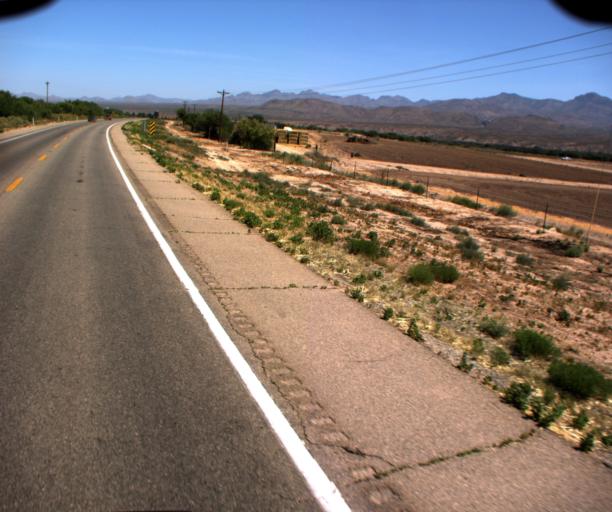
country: US
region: Arizona
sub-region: Graham County
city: Pima
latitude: 33.0228
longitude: -109.9561
